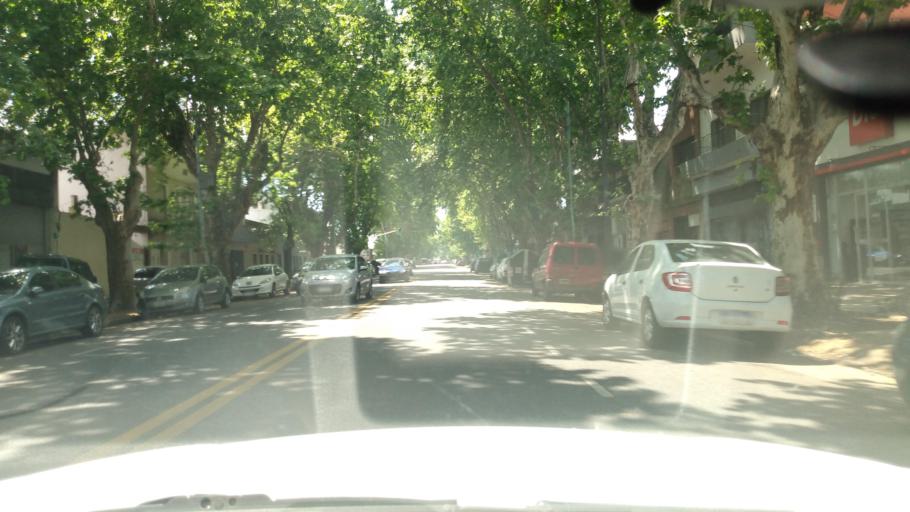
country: AR
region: Buenos Aires
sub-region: Partido de General San Martin
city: General San Martin
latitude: -34.5762
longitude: -58.5074
